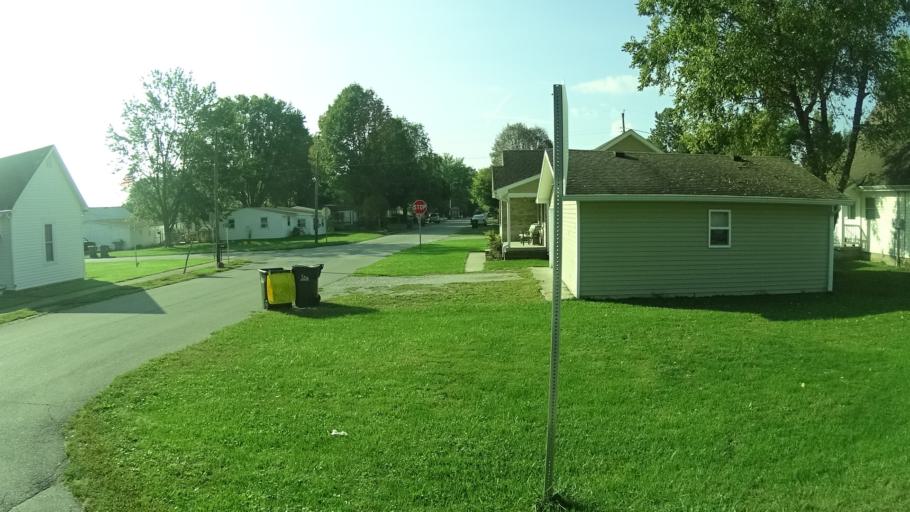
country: US
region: Indiana
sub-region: Madison County
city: Lapel
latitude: 40.0646
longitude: -85.8492
